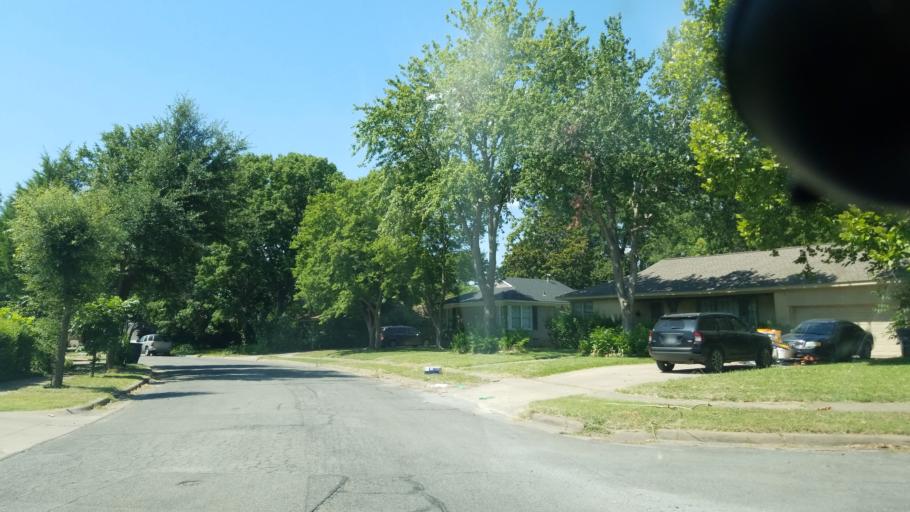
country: US
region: Texas
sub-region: Dallas County
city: Cockrell Hill
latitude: 32.7194
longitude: -96.8392
